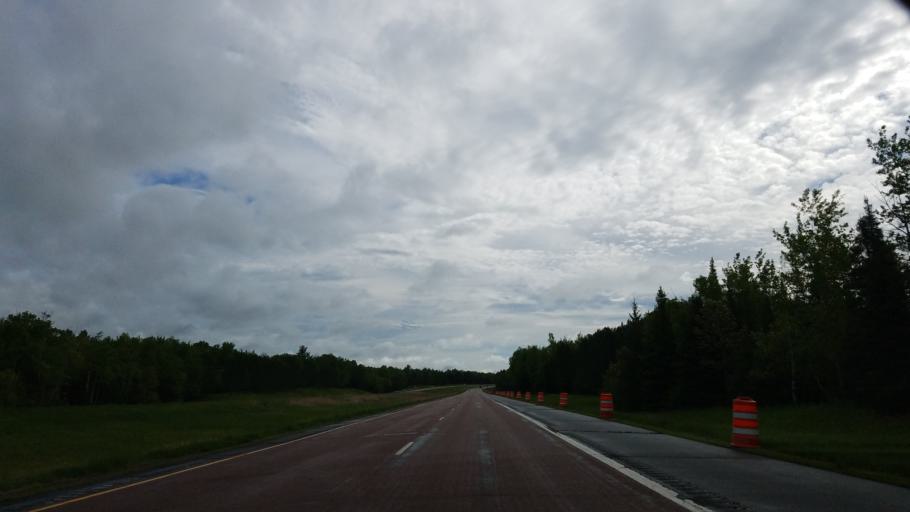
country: US
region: Minnesota
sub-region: Lake County
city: Two Harbors
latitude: 46.9232
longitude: -91.8604
